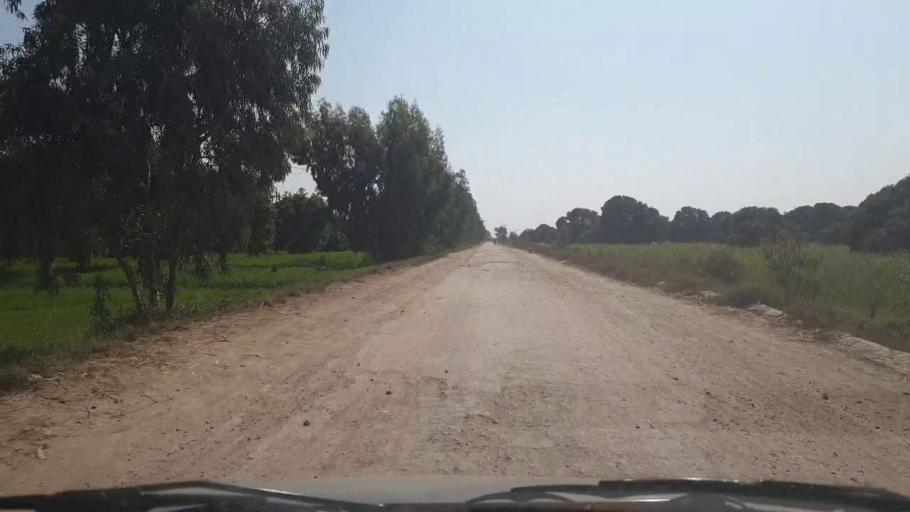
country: PK
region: Sindh
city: Samaro
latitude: 25.2686
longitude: 69.3470
